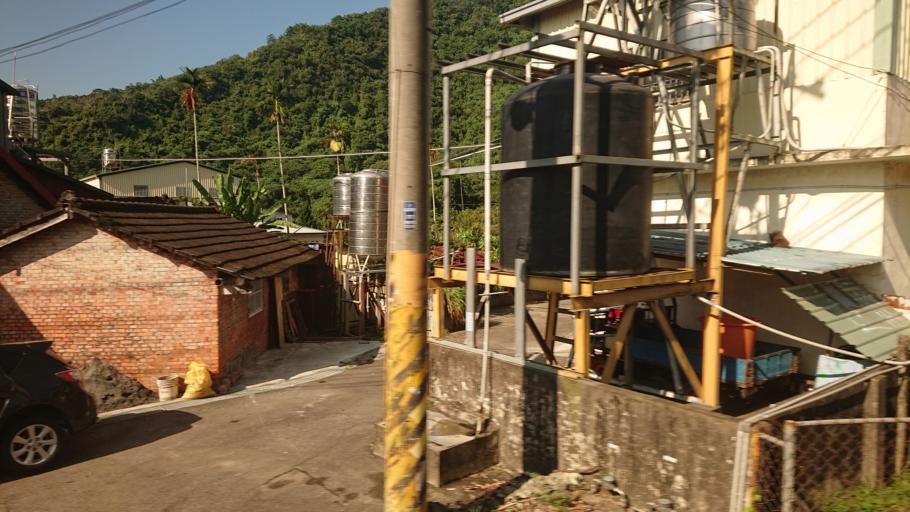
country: TW
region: Taiwan
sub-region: Nantou
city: Puli
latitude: 24.0590
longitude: 120.9022
